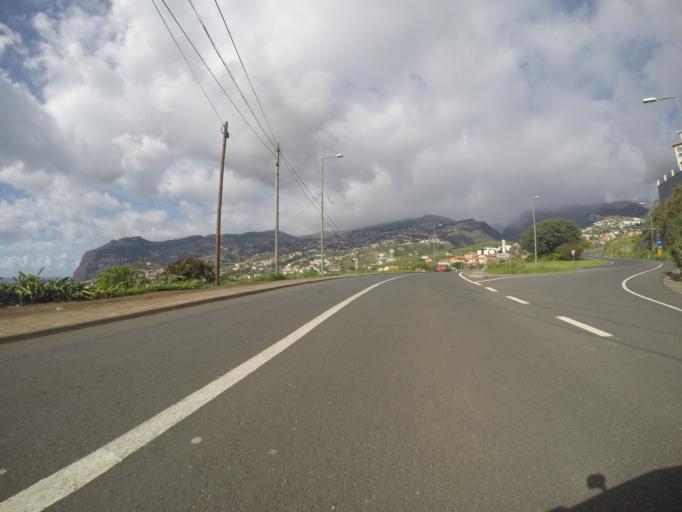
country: PT
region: Madeira
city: Camara de Lobos
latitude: 32.6478
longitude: -16.9579
